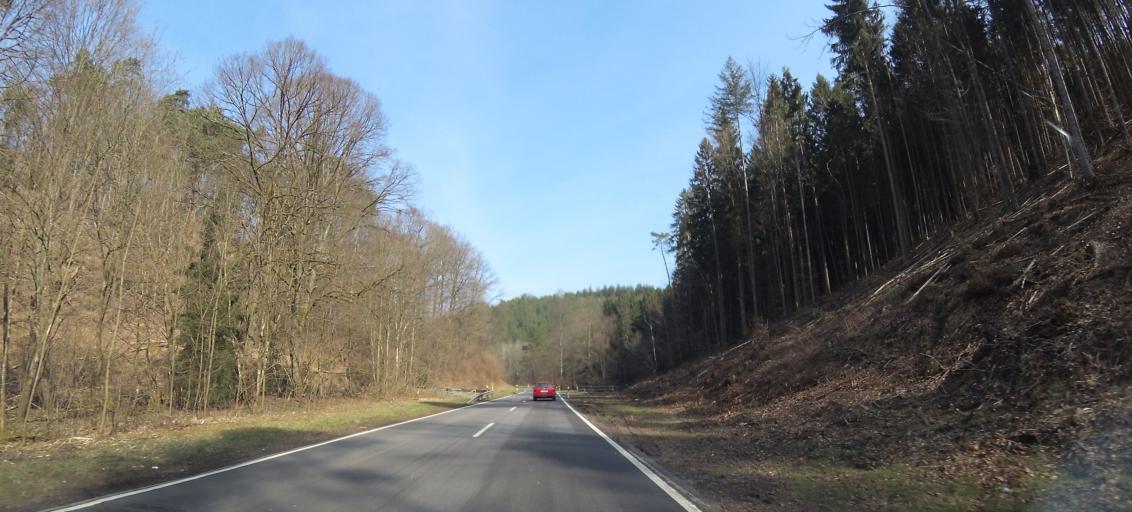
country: DE
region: Rheinland-Pfalz
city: Stelzenberg
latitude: 49.3850
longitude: 7.7375
